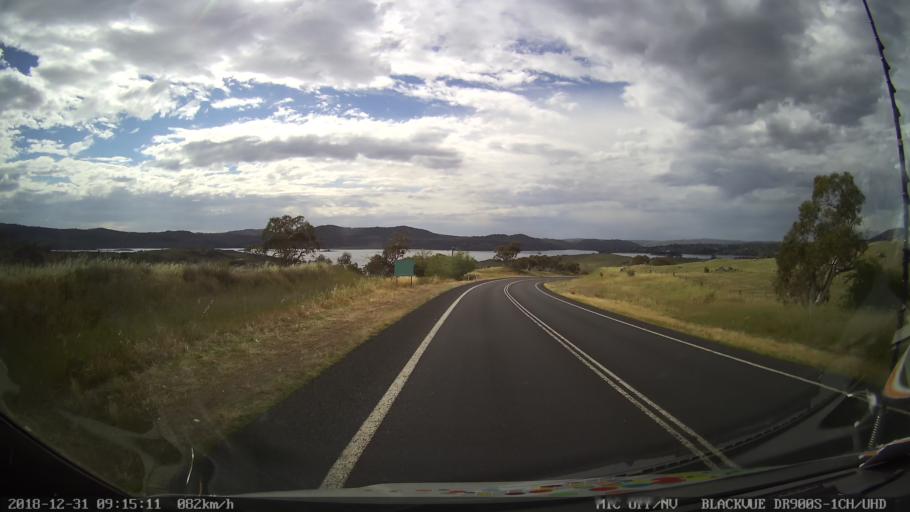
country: AU
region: New South Wales
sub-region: Snowy River
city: Jindabyne
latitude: -36.3822
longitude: 148.5965
